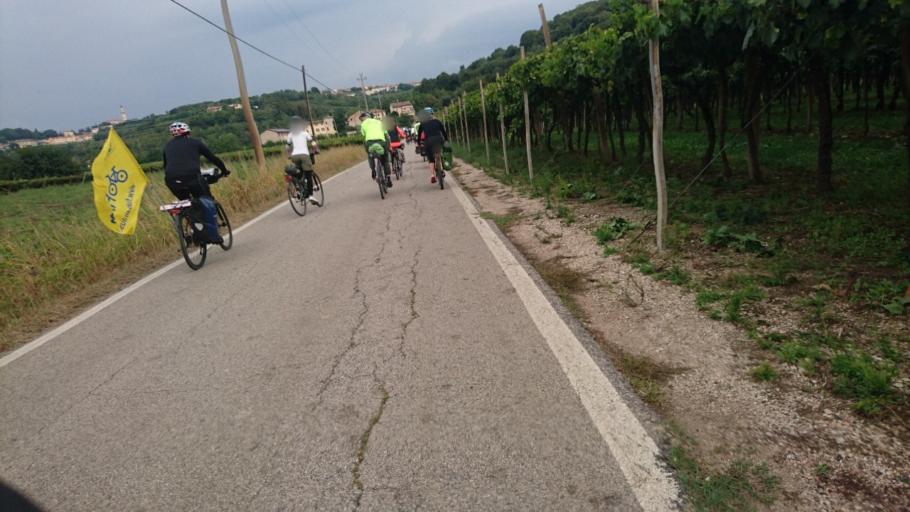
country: IT
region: Veneto
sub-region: Provincia di Verona
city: Colognola ai Colli
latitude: 45.4202
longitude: 11.1970
